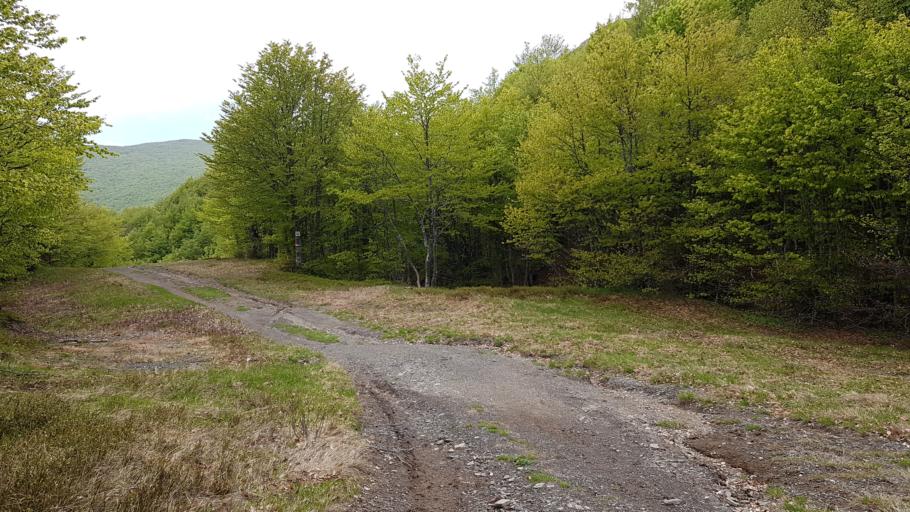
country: IT
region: Liguria
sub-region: Provincia di Genova
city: Santo Stefano d'Aveto
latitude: 44.5597
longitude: 9.4890
